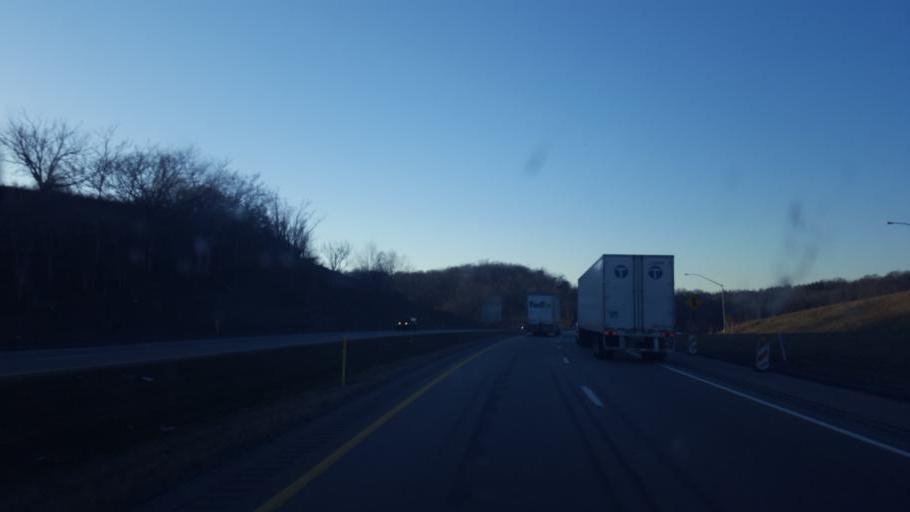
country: US
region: Pennsylvania
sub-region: Washington County
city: East Washington
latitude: 40.1649
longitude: -80.2011
